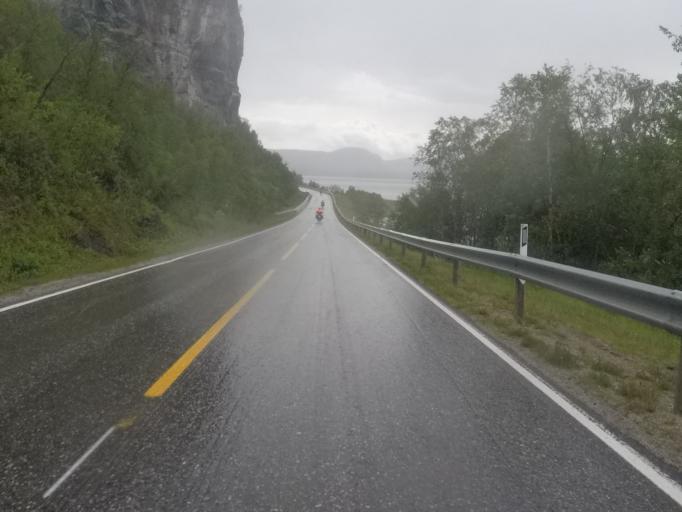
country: NO
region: Finnmark Fylke
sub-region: Porsanger
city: Lakselv
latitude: 69.8574
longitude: 25.0499
